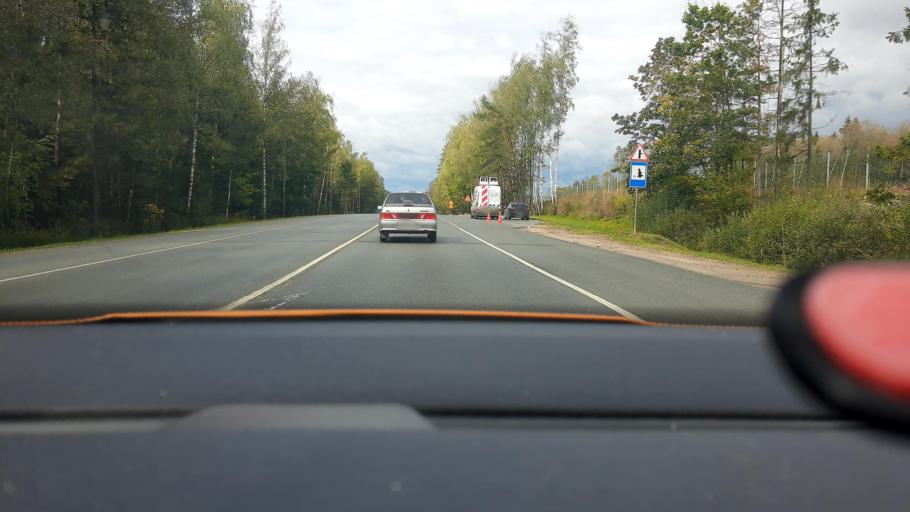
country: RU
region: Moskovskaya
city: Zelenogradskiy
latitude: 56.0951
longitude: 37.9805
